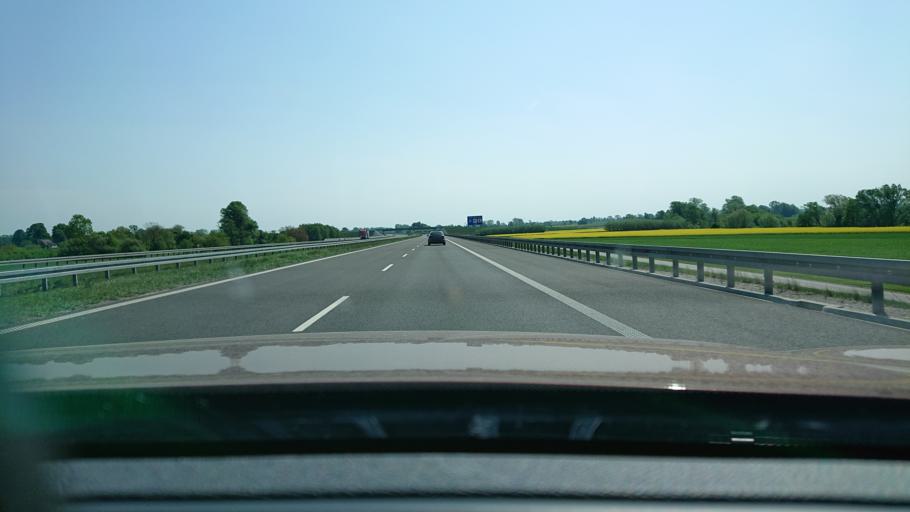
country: PL
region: Subcarpathian Voivodeship
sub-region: Powiat lancucki
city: Rogozno
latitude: 50.1117
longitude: 22.3703
